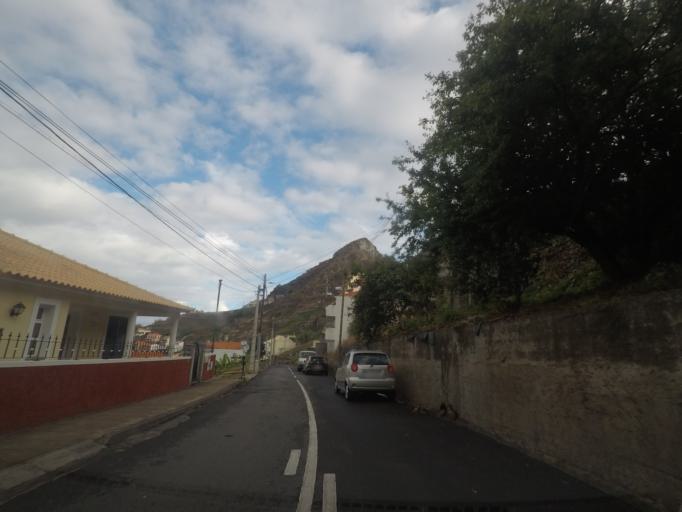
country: PT
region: Madeira
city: Camara de Lobos
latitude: 32.6570
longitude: -16.9970
